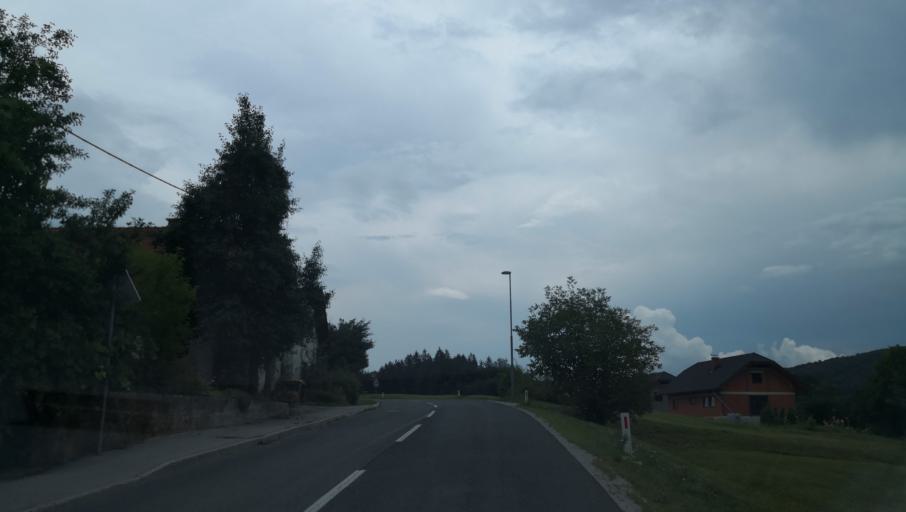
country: SI
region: Ivancna Gorica
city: Ivancna Gorica
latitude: 45.8588
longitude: 14.8377
